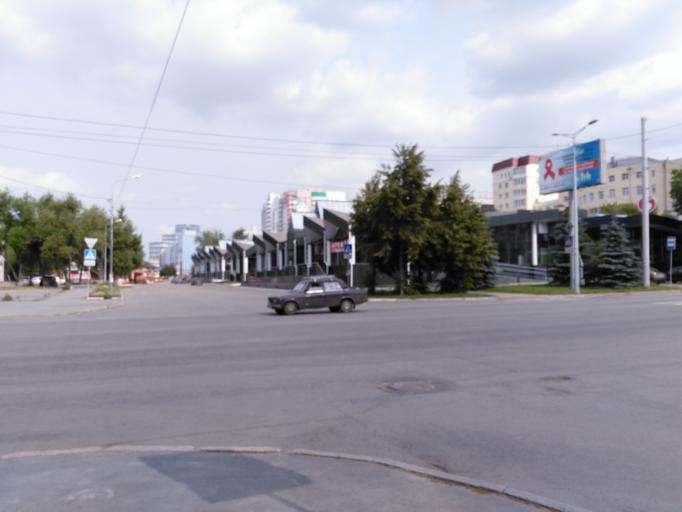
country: RU
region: Chelyabinsk
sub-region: Gorod Chelyabinsk
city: Chelyabinsk
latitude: 55.1639
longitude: 61.4111
